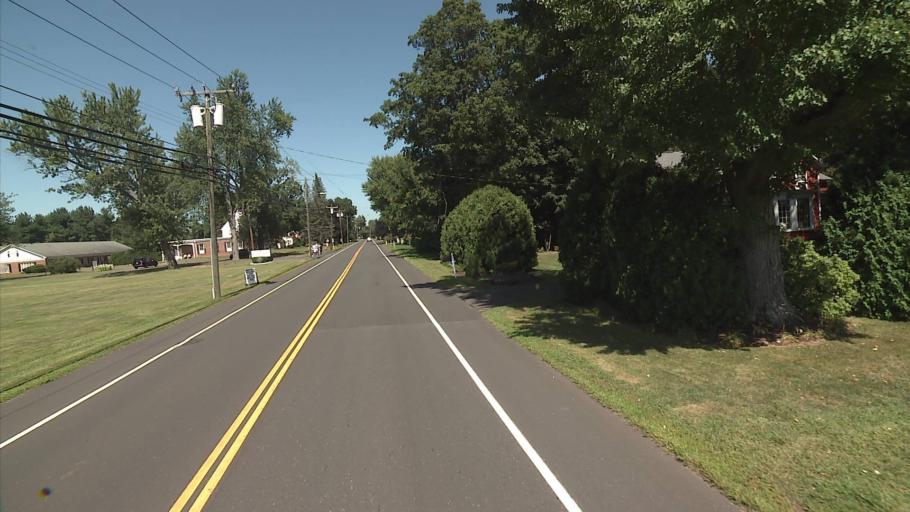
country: US
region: Connecticut
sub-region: Hartford County
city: Windsor
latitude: 41.8702
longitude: -72.6285
